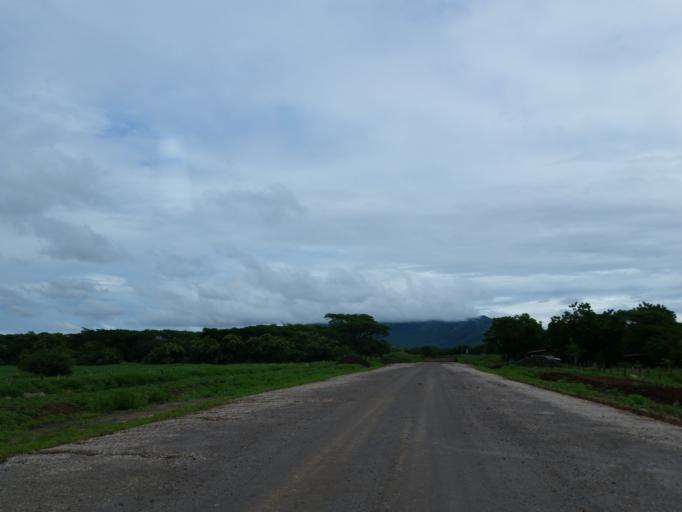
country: NI
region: Leon
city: Larreynaga
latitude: 12.6024
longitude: -86.6722
